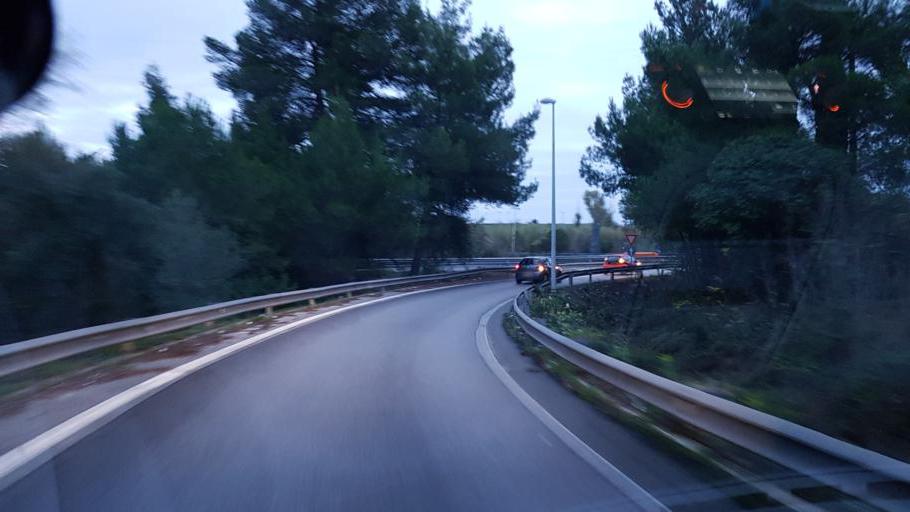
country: IT
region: Apulia
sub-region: Provincia di Taranto
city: Paolo VI
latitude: 40.5063
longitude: 17.2630
